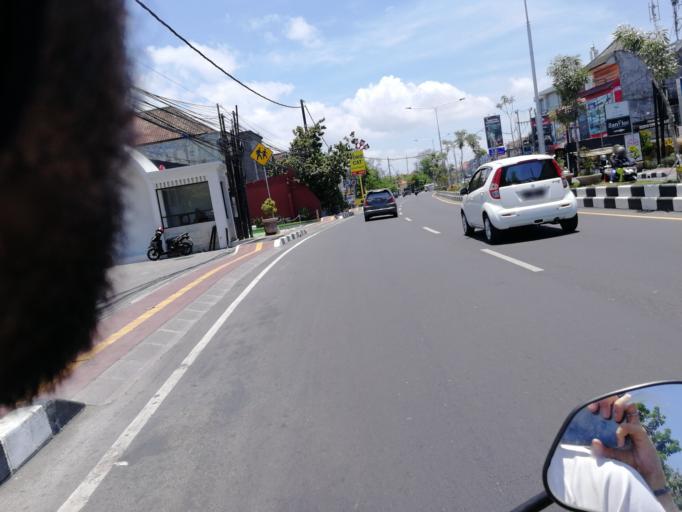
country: ID
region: Bali
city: Kuta
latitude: -8.6974
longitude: 115.1858
